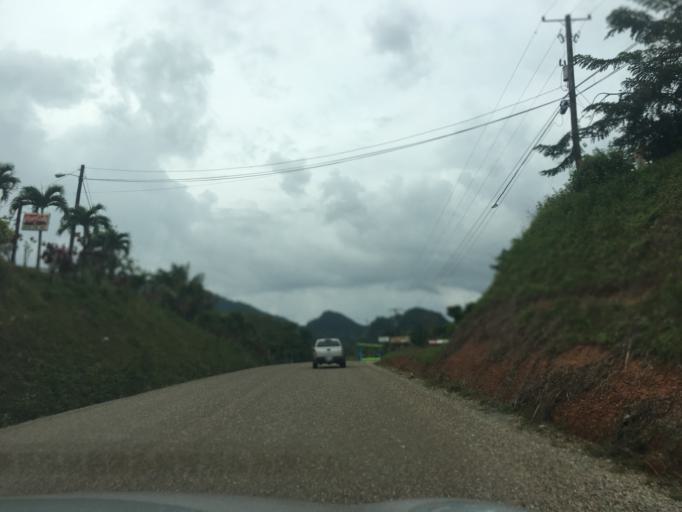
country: BZ
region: Cayo
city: Belmopan
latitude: 17.0882
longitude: -88.6131
